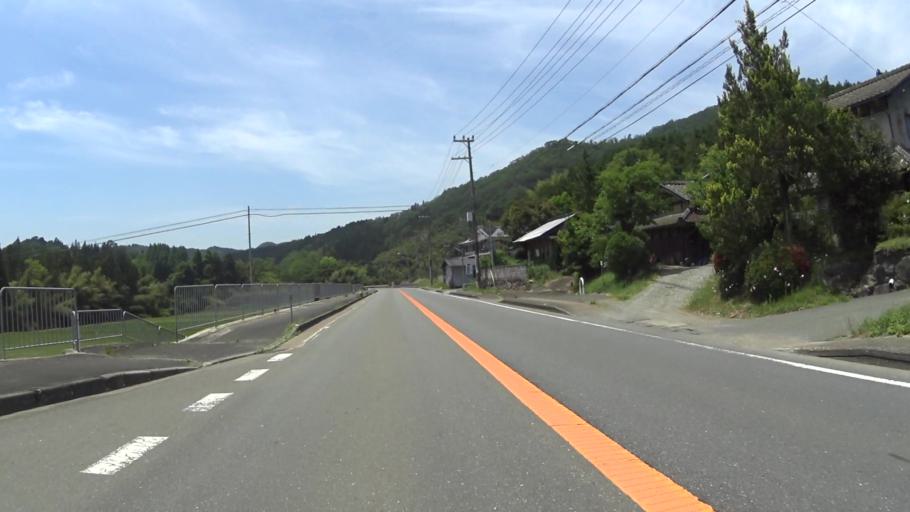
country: JP
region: Kyoto
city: Ayabe
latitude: 35.1899
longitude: 135.3048
